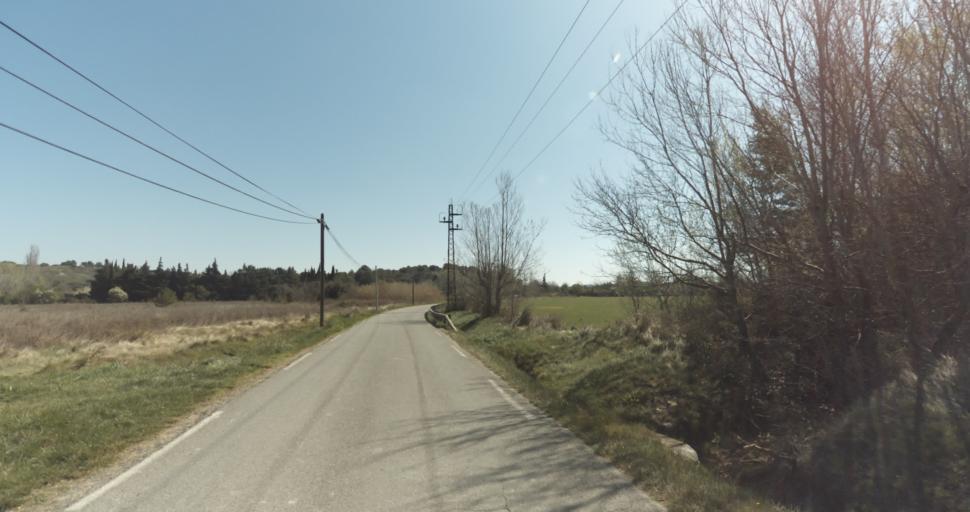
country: FR
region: Provence-Alpes-Cote d'Azur
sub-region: Departement des Bouches-du-Rhone
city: Pelissanne
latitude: 43.6170
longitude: 5.1647
